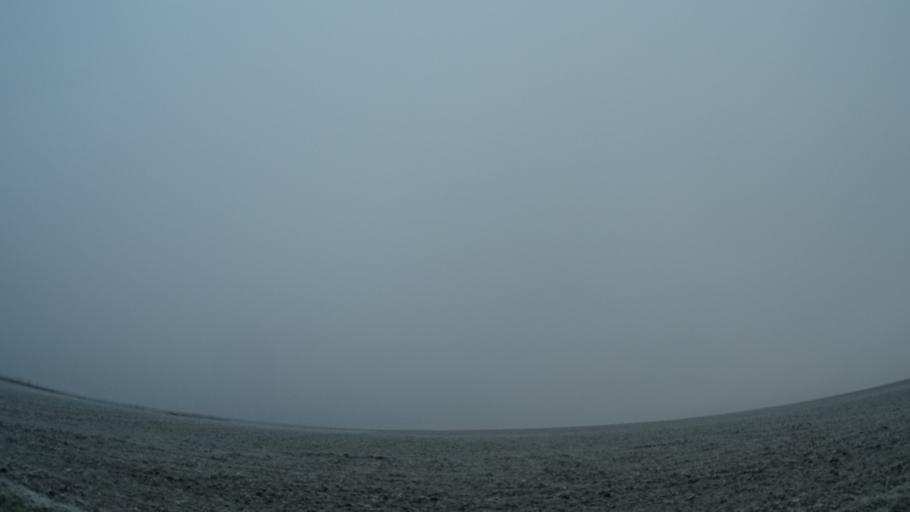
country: DE
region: Bavaria
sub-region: Regierungsbezirk Unterfranken
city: Volkach
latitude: 49.8384
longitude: 10.2740
